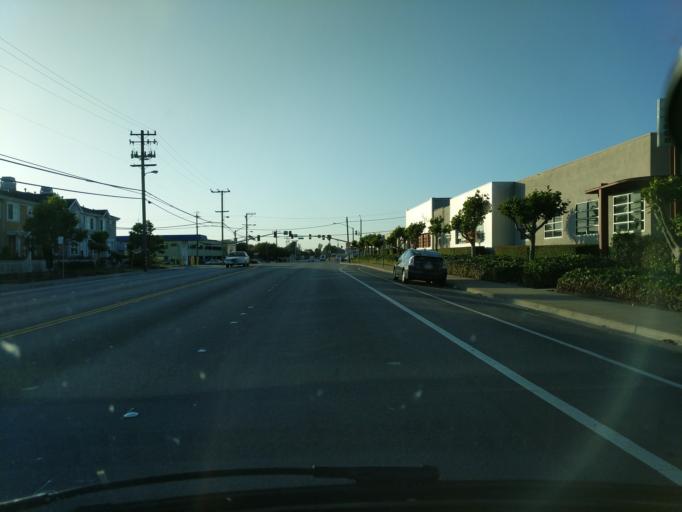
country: US
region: California
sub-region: Alameda County
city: San Leandro
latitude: 37.7072
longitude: -122.1818
